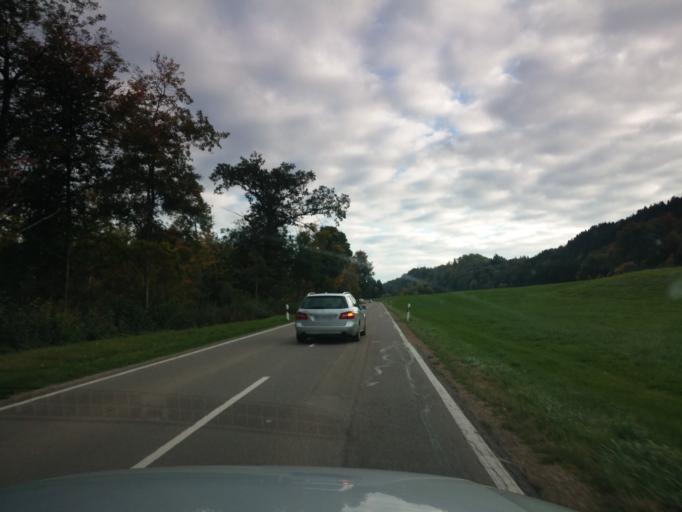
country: DE
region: Baden-Wuerttemberg
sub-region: Tuebingen Region
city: Aitrach
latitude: 47.9571
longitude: 10.0824
